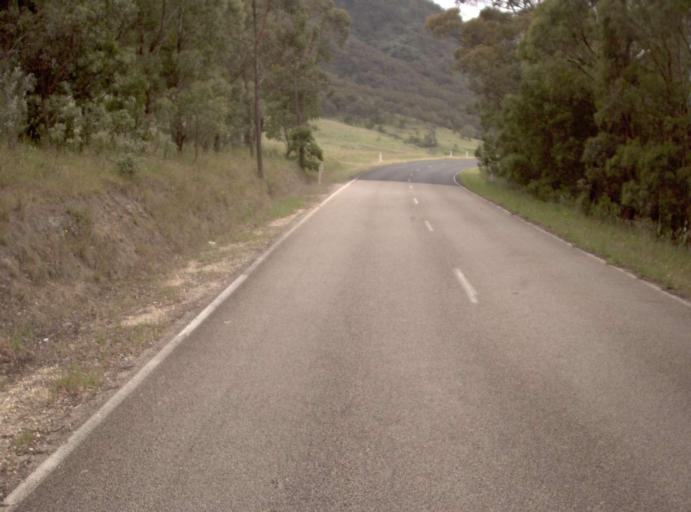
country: AU
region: Victoria
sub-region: East Gippsland
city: Bairnsdale
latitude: -37.5706
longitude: 147.1868
